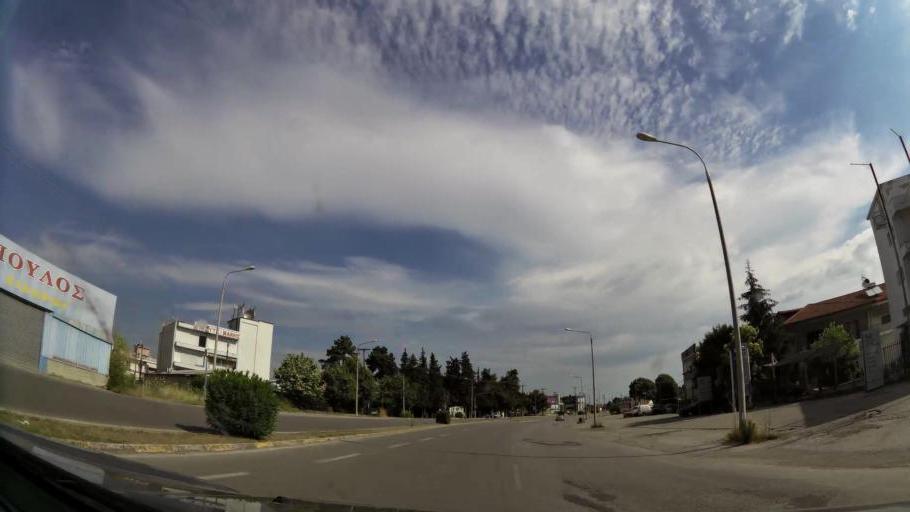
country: GR
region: Central Macedonia
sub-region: Nomos Pierias
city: Katerini
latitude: 40.2798
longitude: 22.5180
